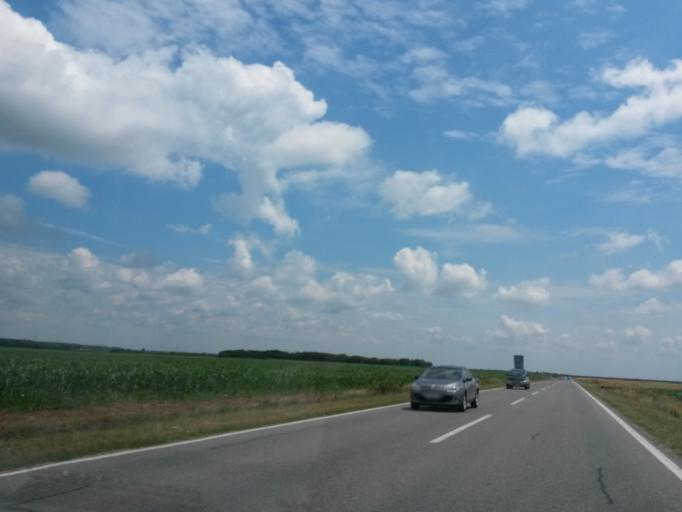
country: HR
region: Osjecko-Baranjska
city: Tenja
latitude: 45.5286
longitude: 18.7487
